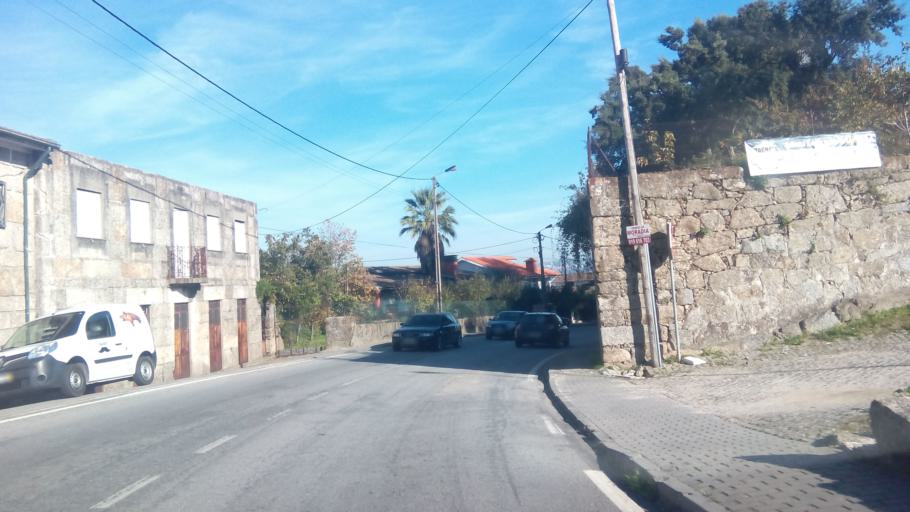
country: PT
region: Porto
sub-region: Paredes
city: Baltar
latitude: 41.1994
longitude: -8.3591
